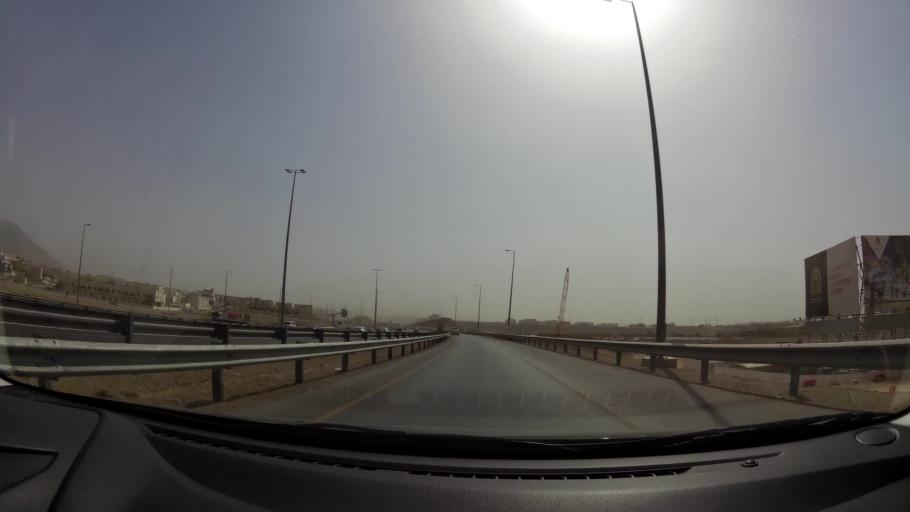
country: OM
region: Muhafazat Masqat
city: Bawshar
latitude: 23.5694
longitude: 58.4023
